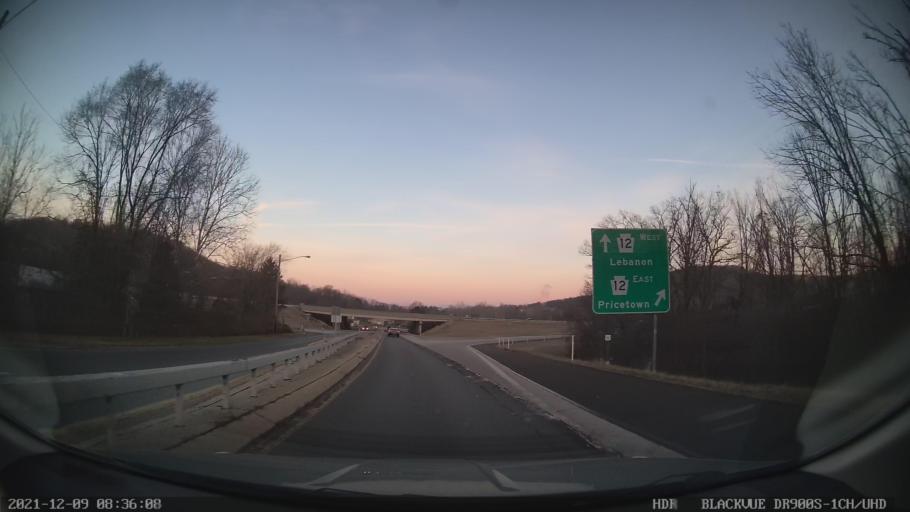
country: US
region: Pennsylvania
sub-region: Berks County
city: Laureldale
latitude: 40.3751
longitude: -75.8974
